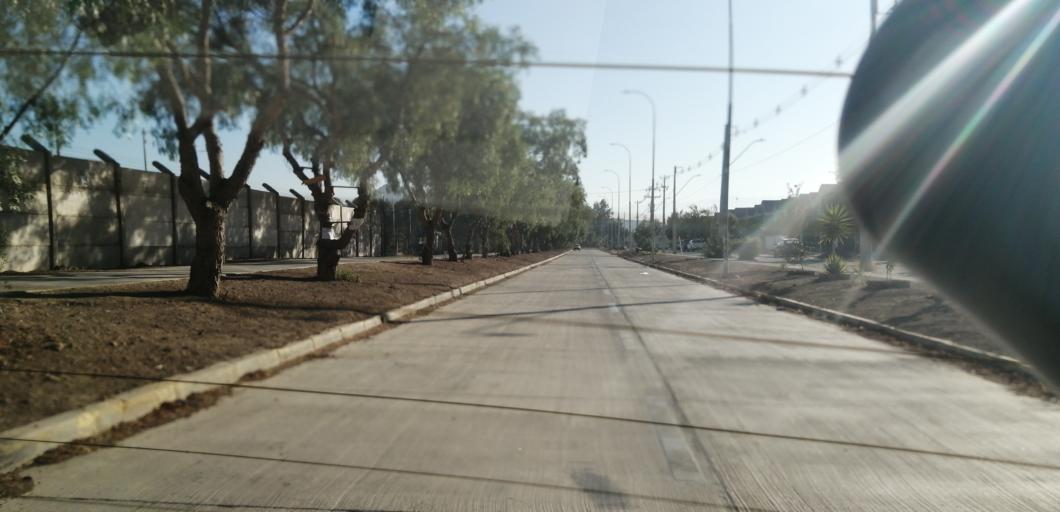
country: CL
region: Santiago Metropolitan
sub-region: Provincia de Santiago
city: Lo Prado
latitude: -33.4478
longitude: -70.8422
